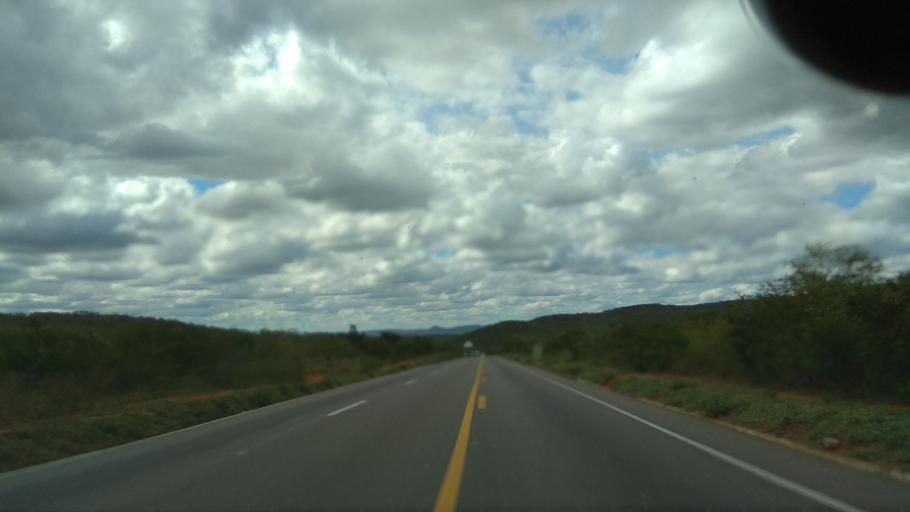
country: BR
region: Bahia
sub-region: Santa Ines
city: Santa Ines
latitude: -13.0343
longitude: -39.9654
